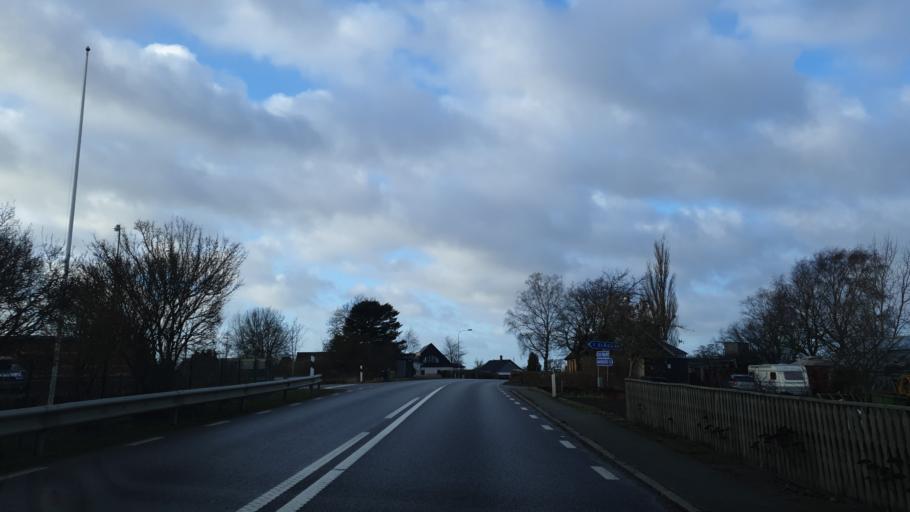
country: SE
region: Skane
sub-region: Trelleborgs Kommun
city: Trelleborg
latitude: 55.4606
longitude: 13.1540
